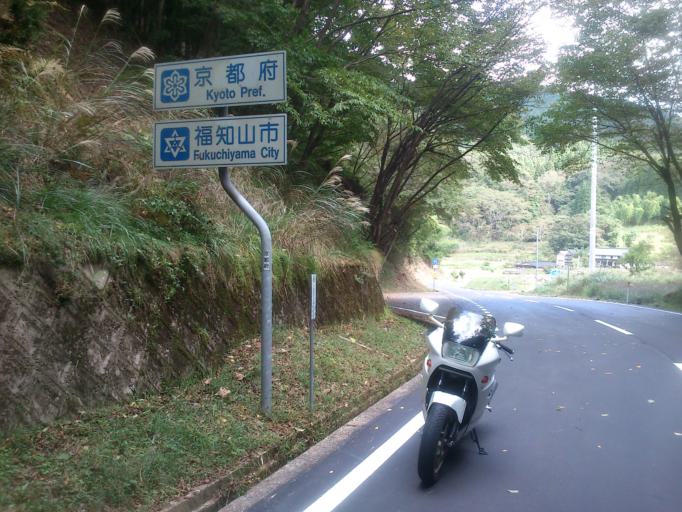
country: JP
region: Kyoto
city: Fukuchiyama
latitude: 35.4298
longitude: 135.0474
